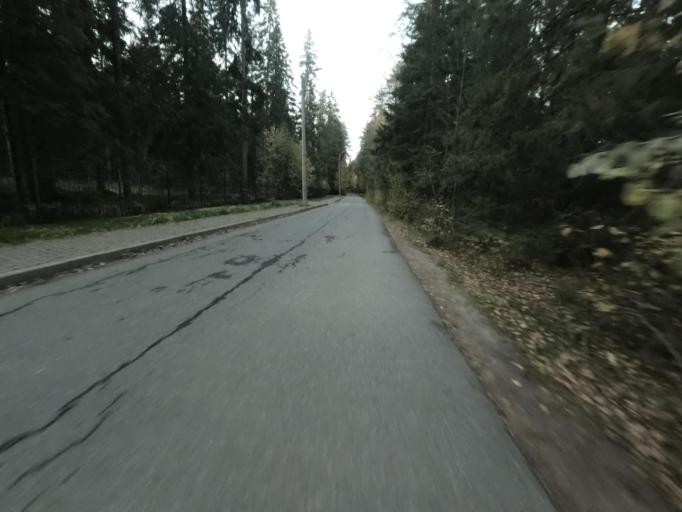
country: RU
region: St.-Petersburg
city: Komarovo
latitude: 60.2045
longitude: 29.8008
